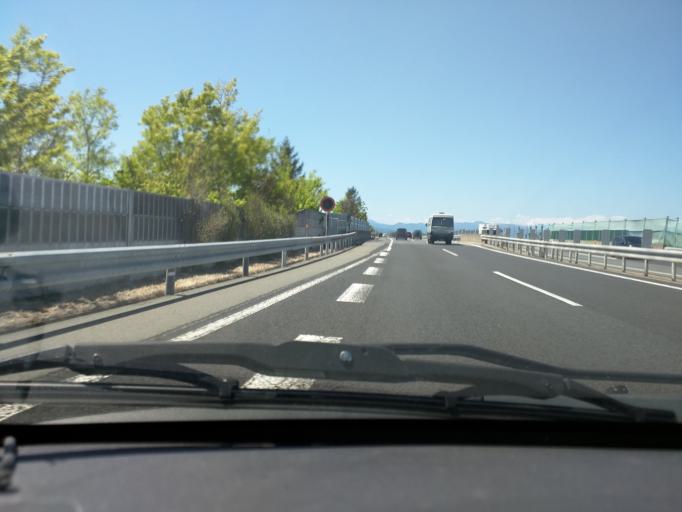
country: JP
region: Nagano
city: Suzaka
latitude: 36.7026
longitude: 138.3018
